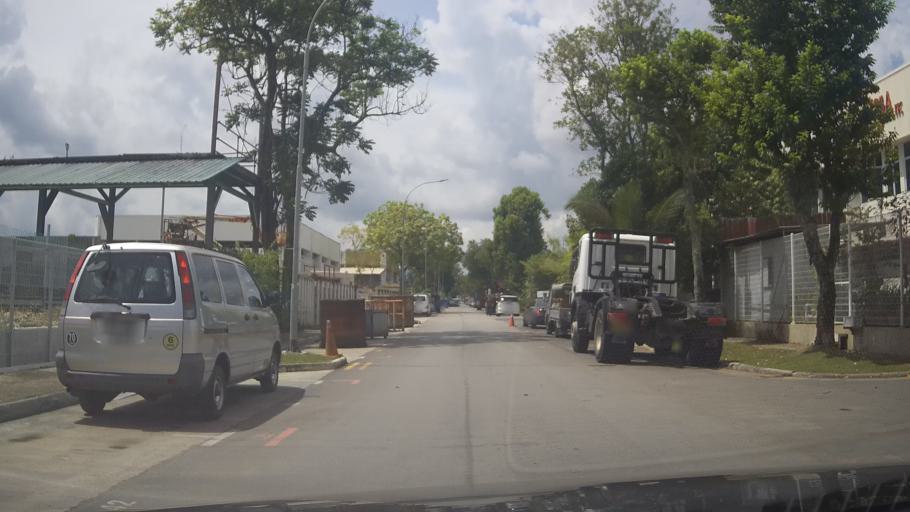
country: MY
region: Johor
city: Johor Bahru
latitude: 1.4533
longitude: 103.7991
